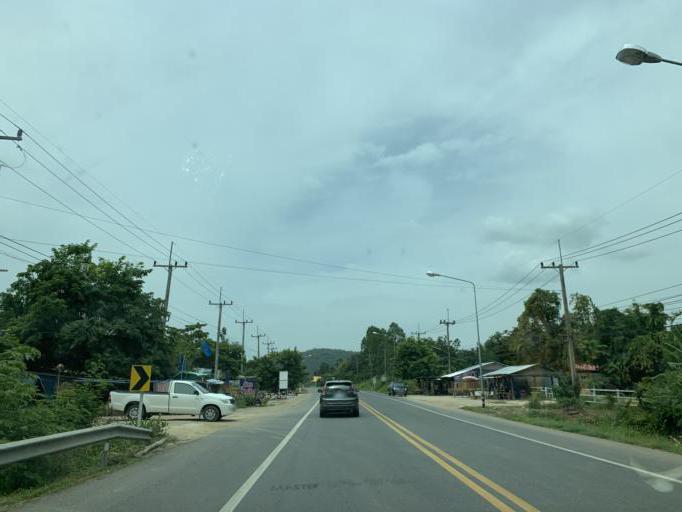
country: TH
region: Uthai Thani
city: Uthai Thani
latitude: 15.4124
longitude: 99.9977
